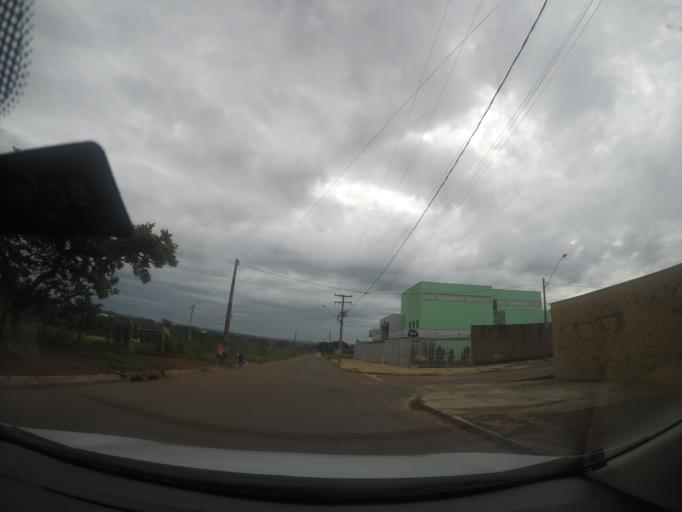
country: BR
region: Goias
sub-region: Goiania
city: Goiania
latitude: -16.6437
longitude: -49.3366
